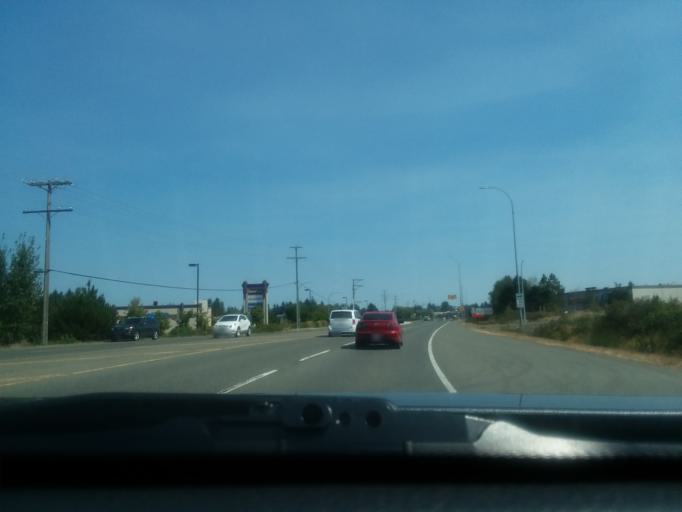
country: CA
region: British Columbia
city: Nanaimo
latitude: 49.2411
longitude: -124.0581
